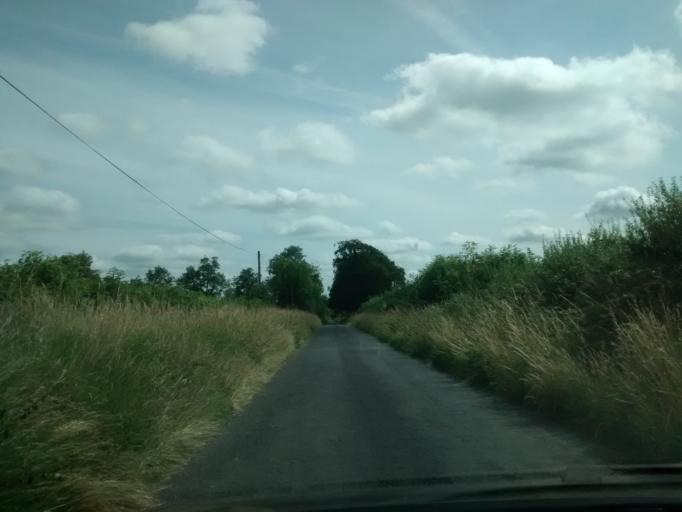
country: IE
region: Leinster
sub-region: Uibh Fhaili
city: Clara
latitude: 53.3674
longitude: -7.6318
